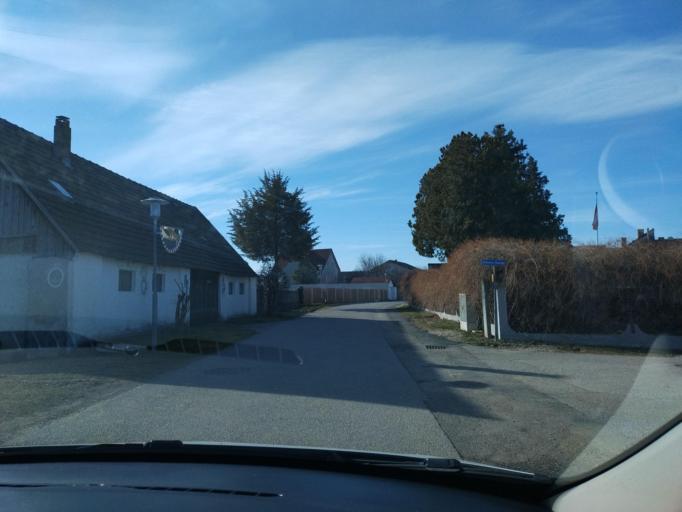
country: AT
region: Lower Austria
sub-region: Politischer Bezirk Wiener Neustadt
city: Lanzenkirchen
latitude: 47.7428
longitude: 16.2375
